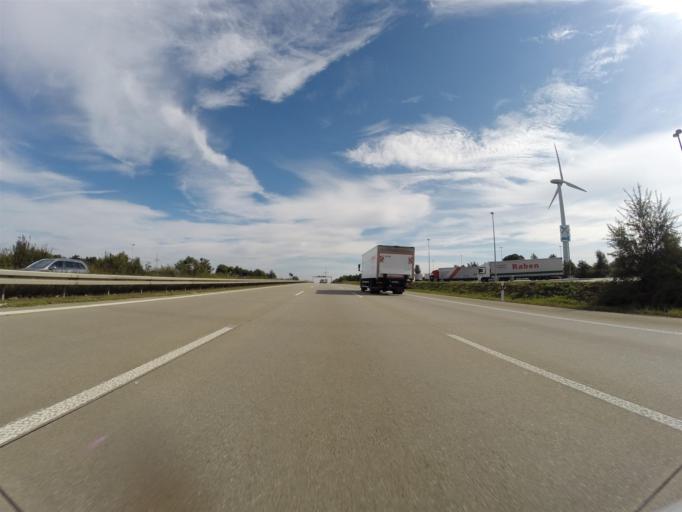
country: DE
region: Saxony
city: Wilsdruff
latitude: 51.0617
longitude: 13.5718
